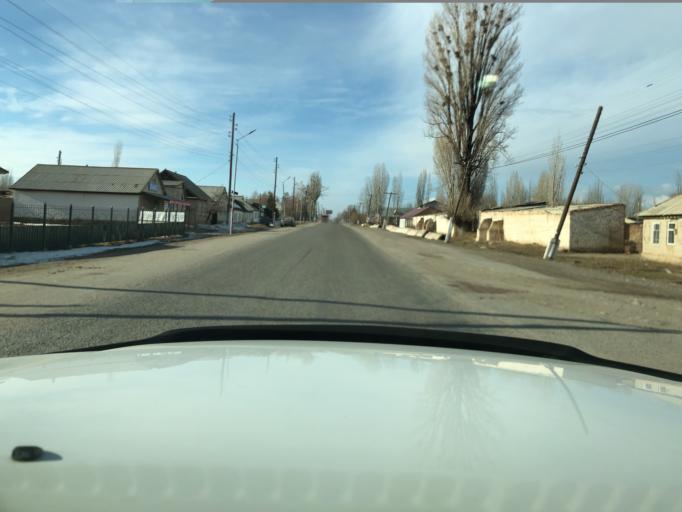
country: KG
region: Ysyk-Koel
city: Pokrovka
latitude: 42.3232
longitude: 77.9283
